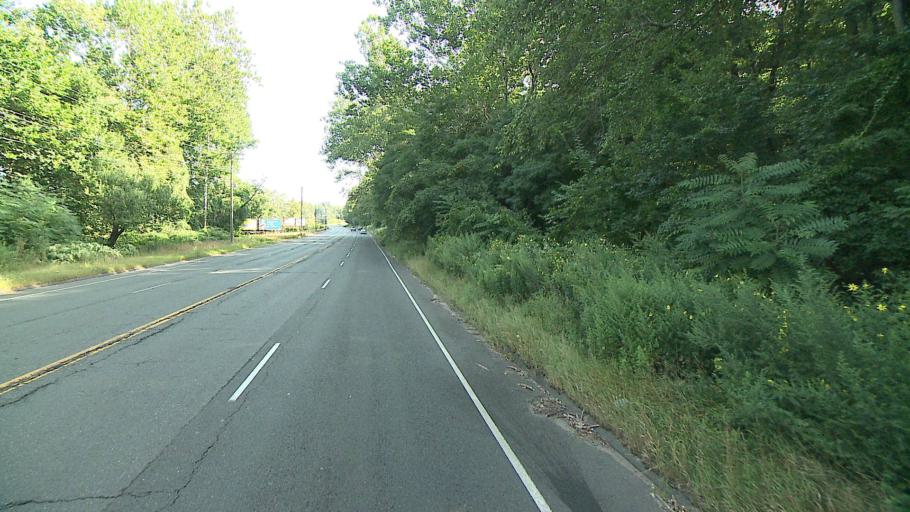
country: US
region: Connecticut
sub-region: New Haven County
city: Naugatuck
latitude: 41.5187
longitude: -73.0442
